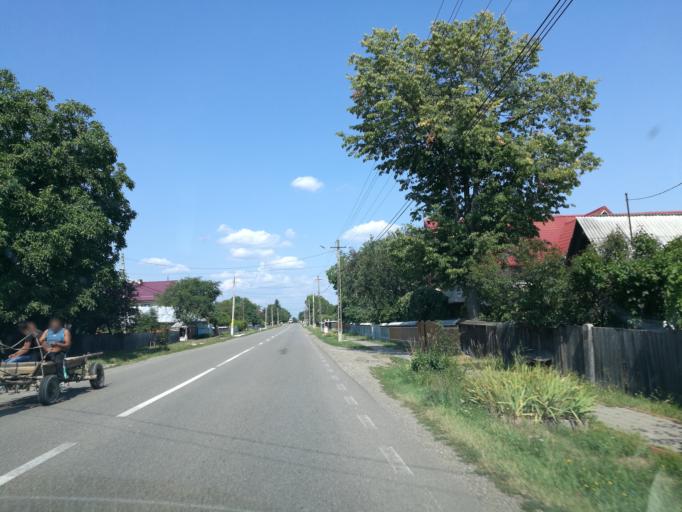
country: RO
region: Neamt
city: Bodesti
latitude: 47.0331
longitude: 26.4145
